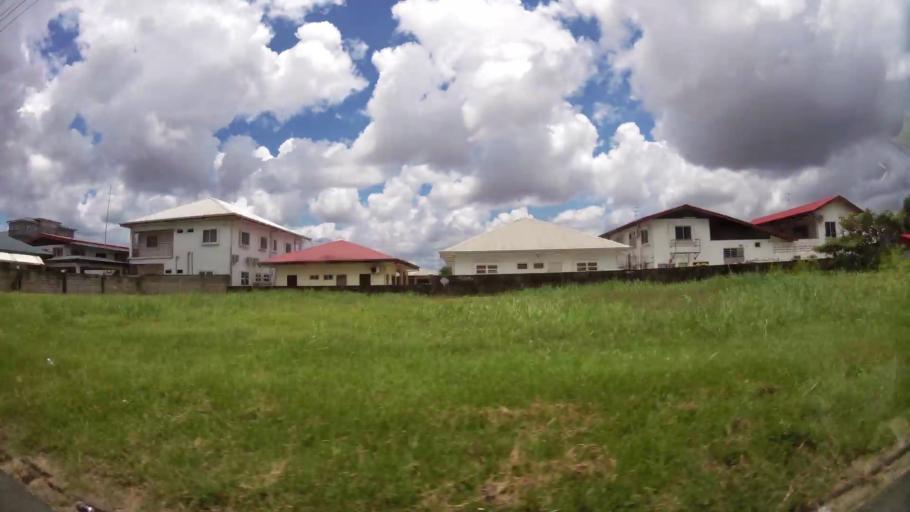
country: SR
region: Paramaribo
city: Paramaribo
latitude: 5.8519
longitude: -55.1398
